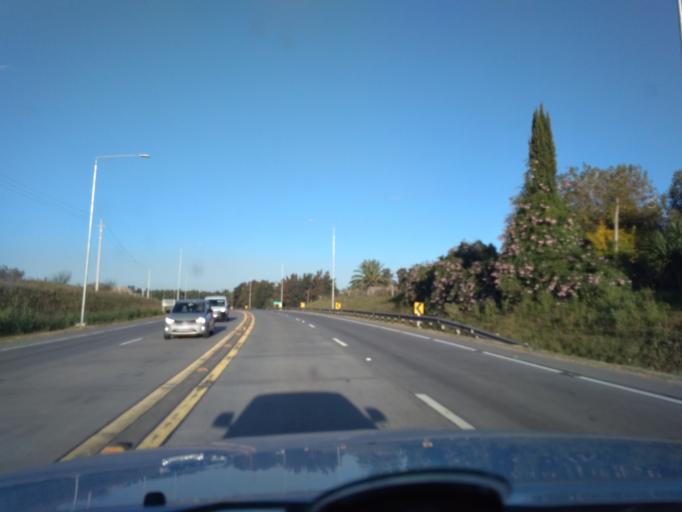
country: UY
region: Canelones
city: La Paz
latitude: -34.7832
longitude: -56.2501
